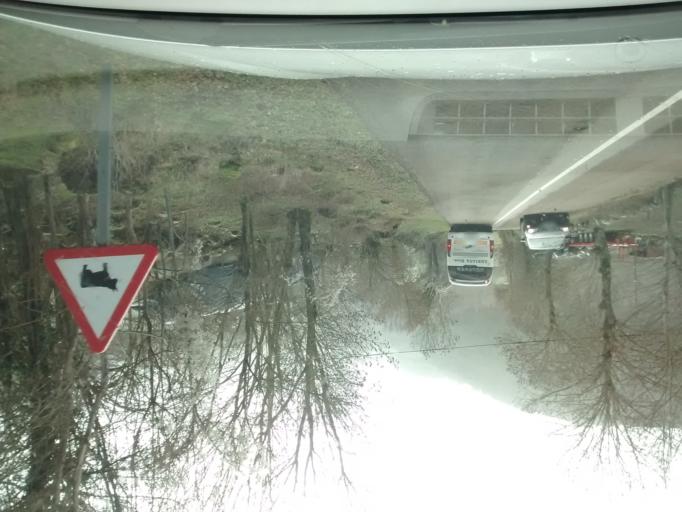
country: ES
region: Castille and Leon
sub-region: Provincia de Burgos
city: Espinosa de los Monteros
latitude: 43.1196
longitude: -3.5989
